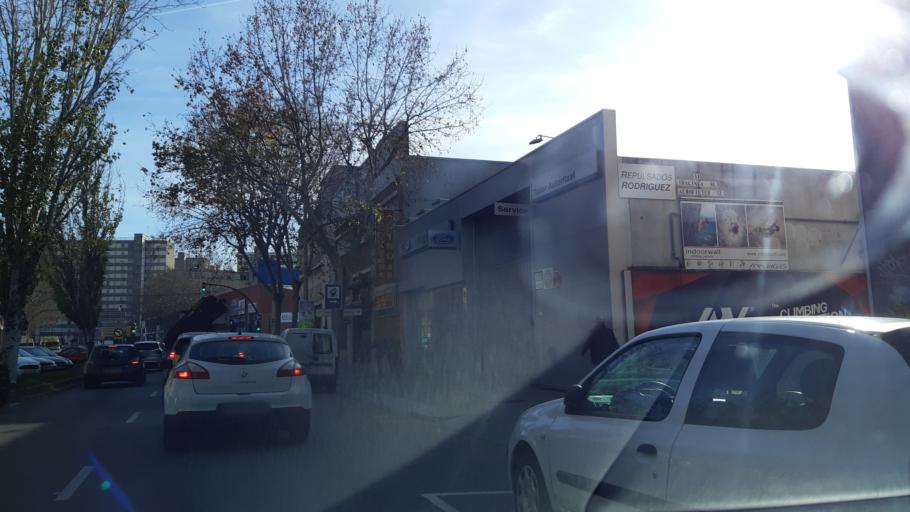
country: ES
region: Catalonia
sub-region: Provincia de Barcelona
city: L'Hospitalet de Llobregat
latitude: 41.3573
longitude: 2.1091
